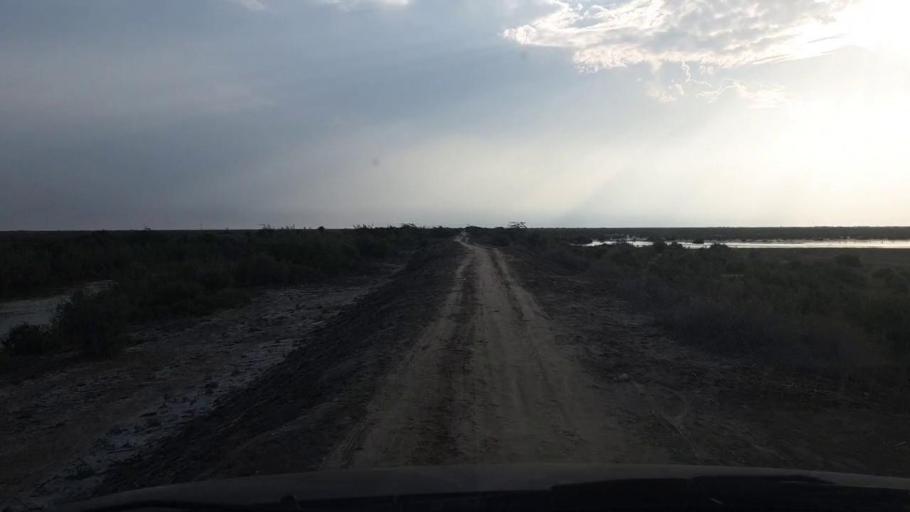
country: PK
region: Sindh
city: Badin
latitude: 24.4387
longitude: 68.6744
